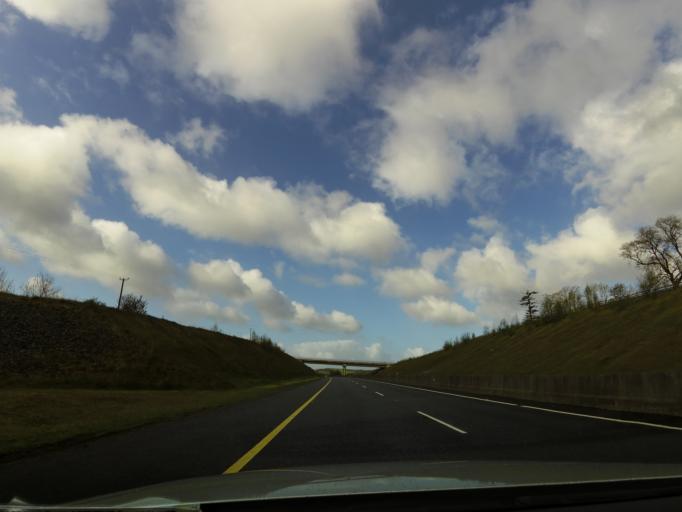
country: IE
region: Munster
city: Ballina
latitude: 52.7843
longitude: -8.3671
